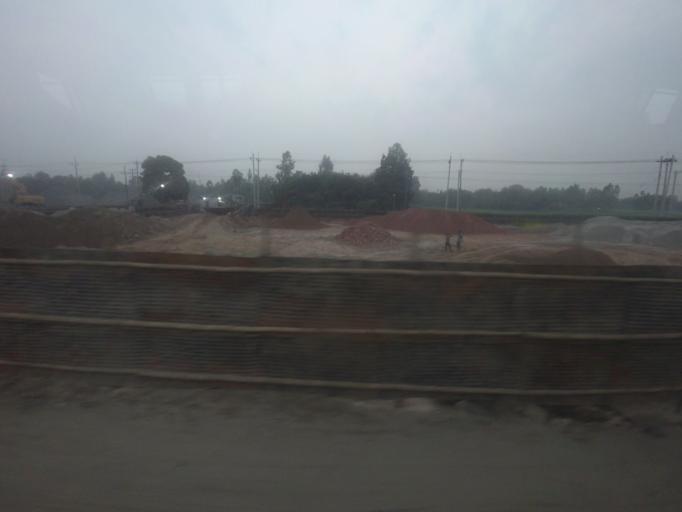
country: BD
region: Dhaka
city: Tangail
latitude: 24.3200
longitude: 89.9246
